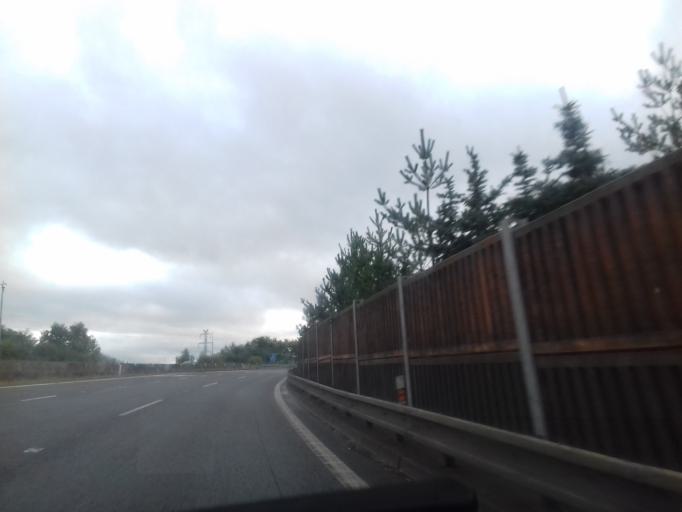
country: CZ
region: Liberecky
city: Hodkovice nad Mohelkou
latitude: 50.6348
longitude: 15.1104
